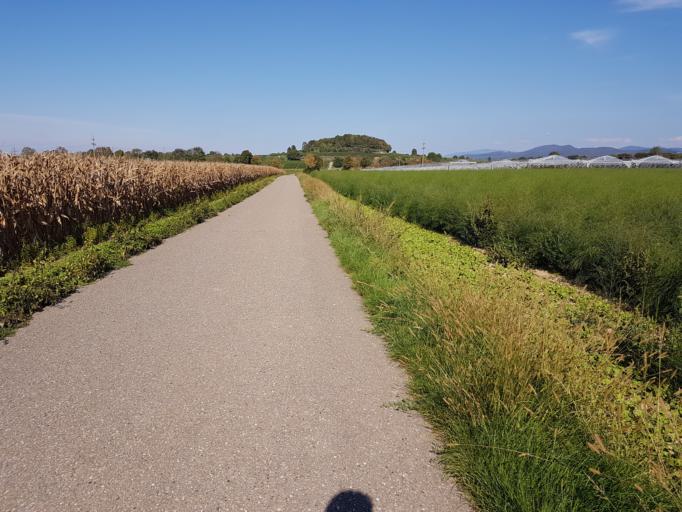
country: DE
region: Baden-Wuerttemberg
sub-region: Freiburg Region
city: Unterkrozingen
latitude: 47.9071
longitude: 7.6734
